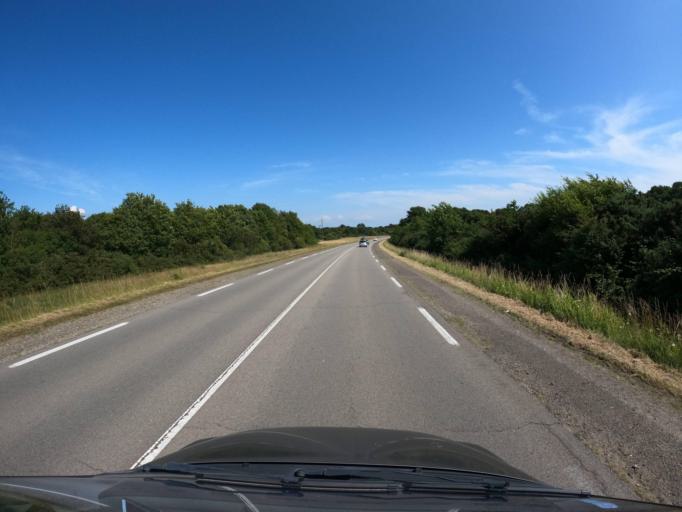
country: FR
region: Pays de la Loire
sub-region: Departement de la Loire-Atlantique
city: La Bernerie-en-Retz
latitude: 47.1024
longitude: -2.0419
